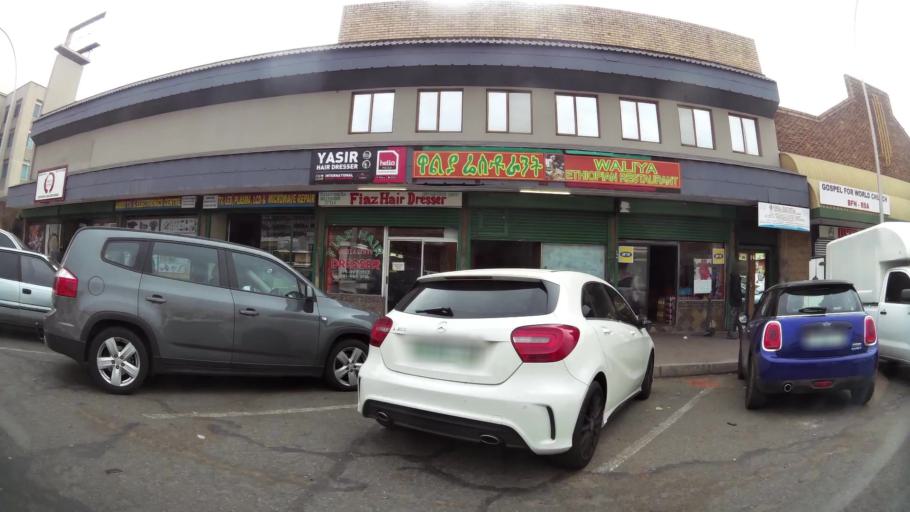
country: ZA
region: Orange Free State
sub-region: Mangaung Metropolitan Municipality
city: Bloemfontein
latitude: -29.1158
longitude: 26.2242
